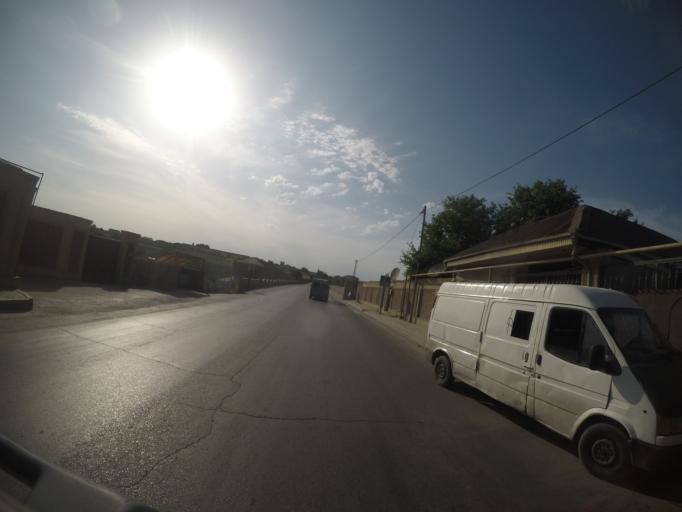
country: AZ
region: Baki
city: Binagadi
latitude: 40.4689
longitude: 49.8403
